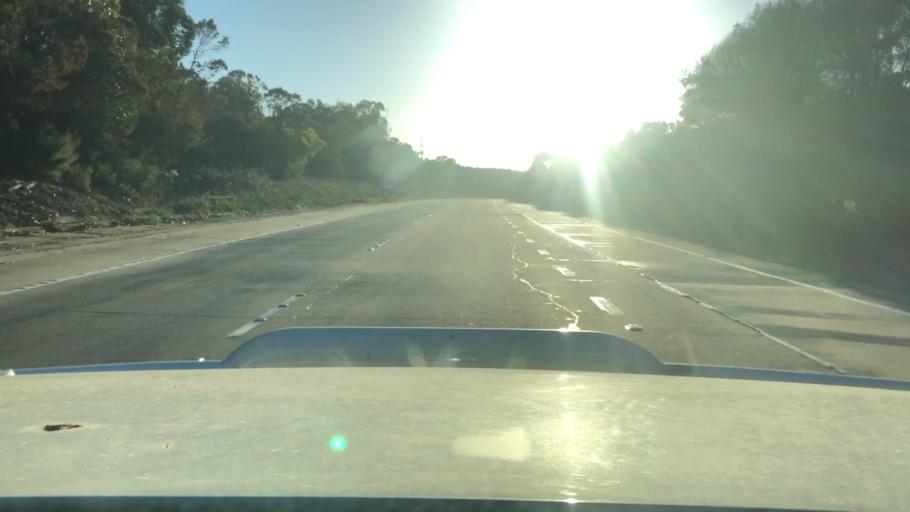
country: AU
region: New South Wales
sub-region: Wingecarribee
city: Bundanoon
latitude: -34.6950
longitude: 150.0252
